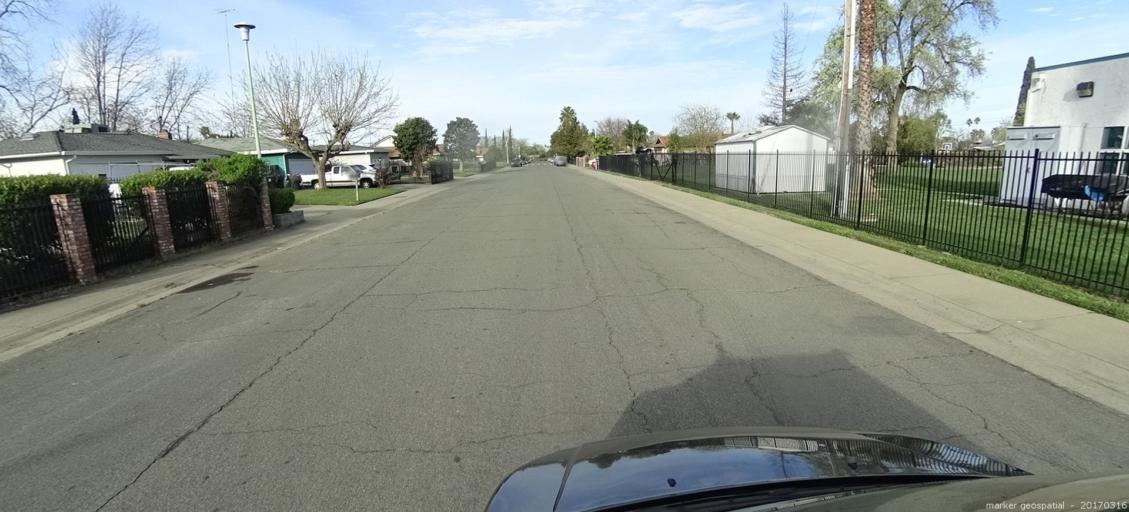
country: US
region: California
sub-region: Sacramento County
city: Parkway
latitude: 38.5057
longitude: -121.4791
